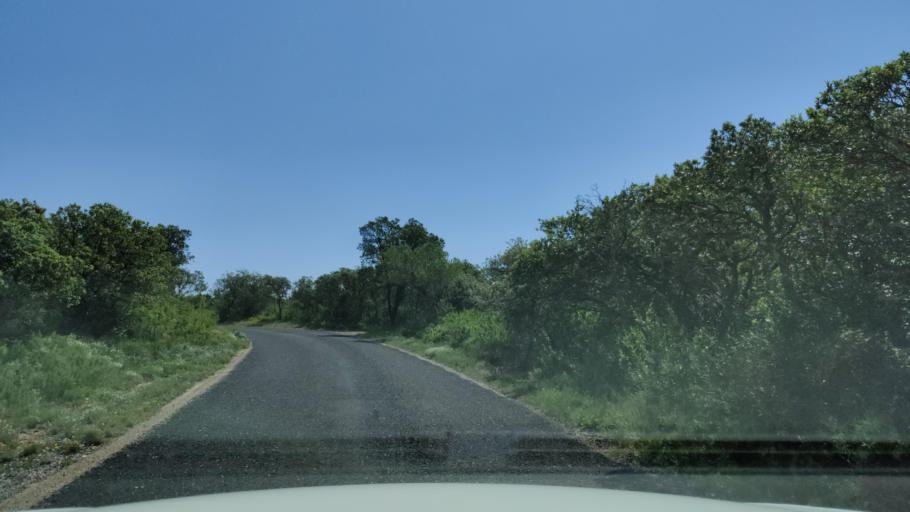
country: FR
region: Languedoc-Roussillon
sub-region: Departement des Pyrenees-Orientales
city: Estagel
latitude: 42.7893
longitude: 2.7344
